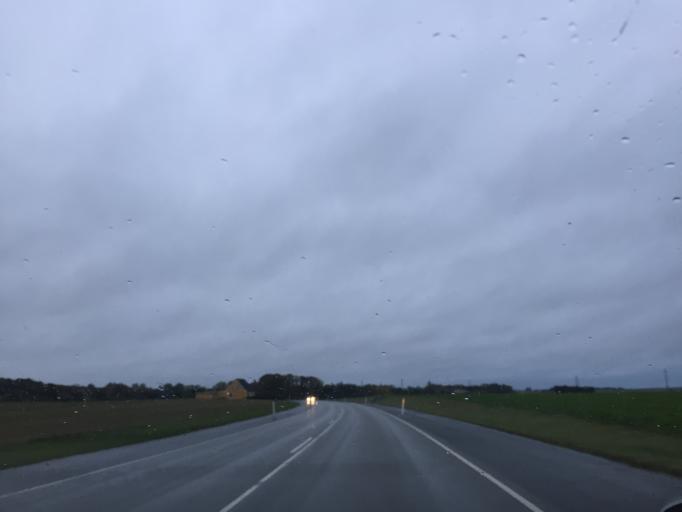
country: DK
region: Zealand
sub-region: Ringsted Kommune
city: Ringsted
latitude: 55.4726
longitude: 11.7420
